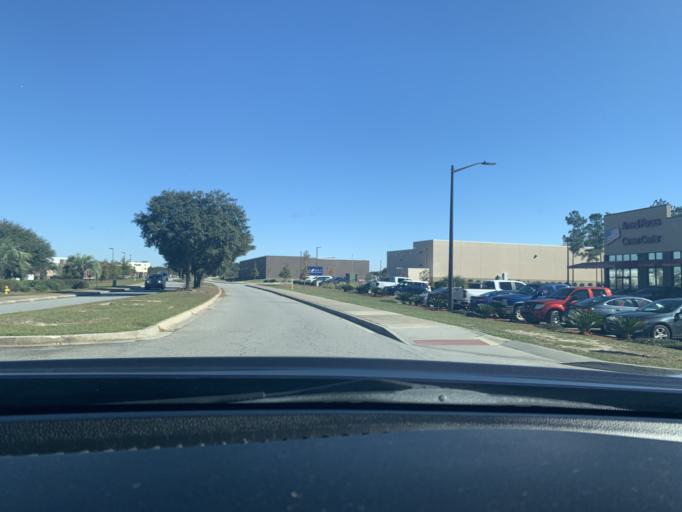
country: US
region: Georgia
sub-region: Chatham County
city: Pooler
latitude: 32.1404
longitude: -81.2547
